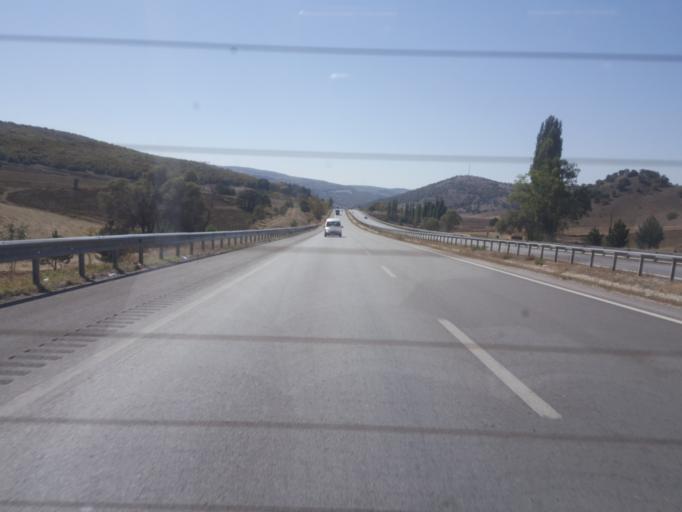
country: TR
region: Corum
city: Alaca
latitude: 40.2848
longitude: 34.6479
